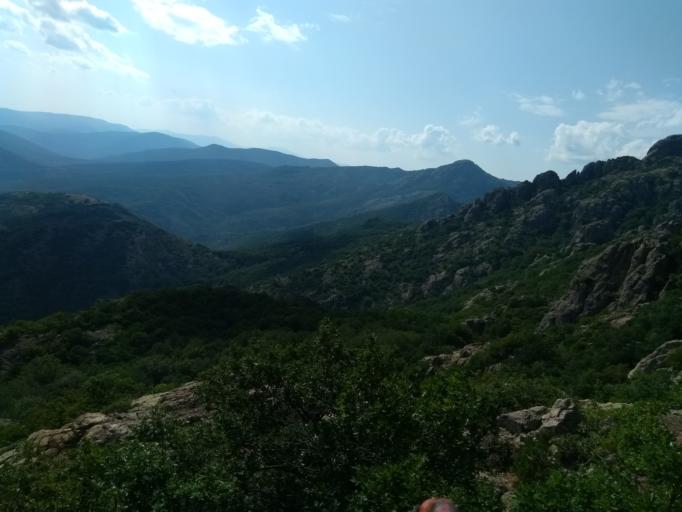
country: BG
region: Sliven
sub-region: Obshtina Sliven
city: Sliven
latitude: 42.7163
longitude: 26.3580
